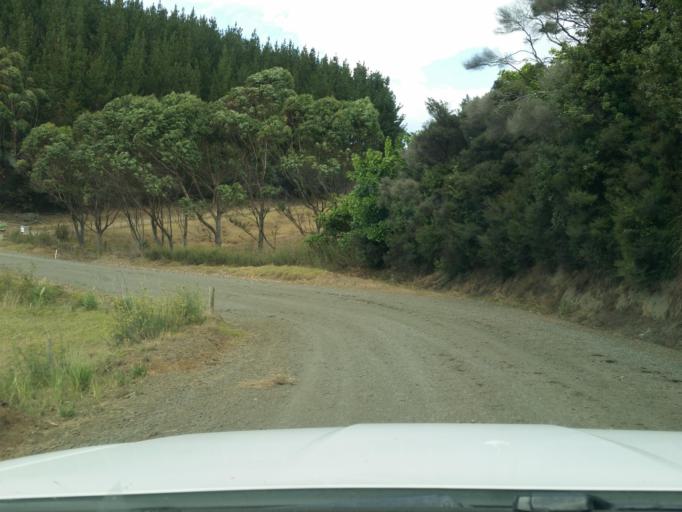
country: NZ
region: Auckland
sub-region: Auckland
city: Wellsford
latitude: -36.3344
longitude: 174.1557
